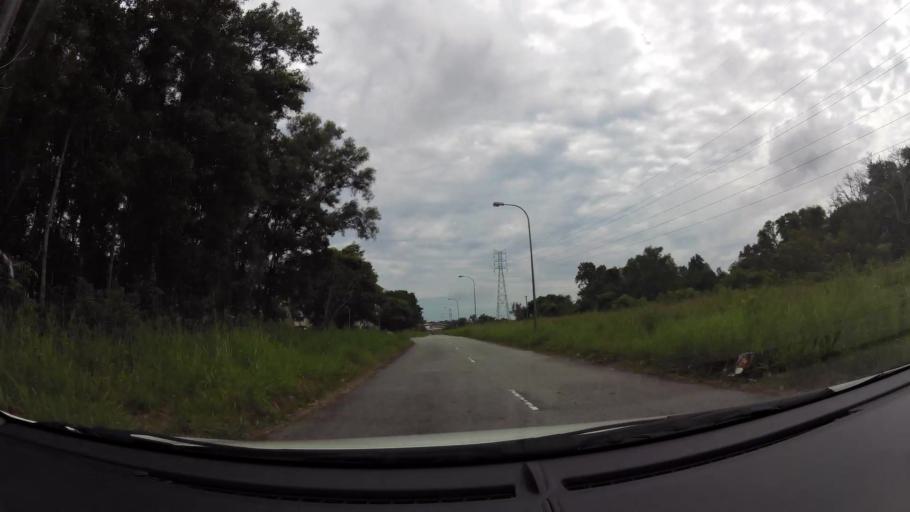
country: BN
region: Brunei and Muara
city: Bandar Seri Begawan
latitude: 4.8990
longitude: 114.9050
